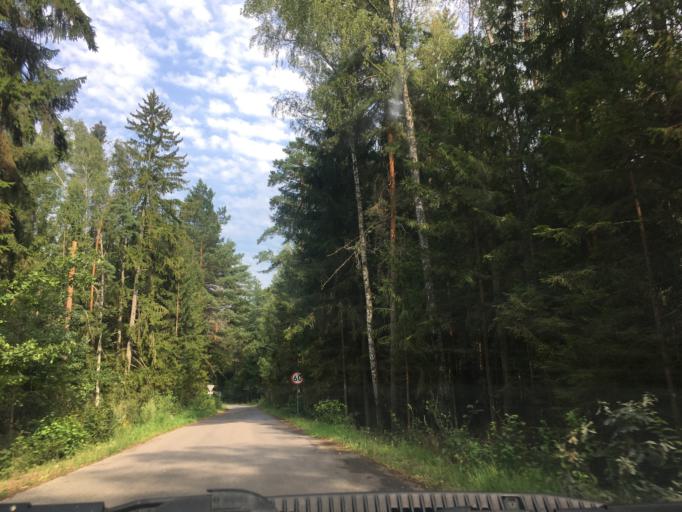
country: PL
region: Podlasie
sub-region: Powiat hajnowski
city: Bialowieza
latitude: 52.8820
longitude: 23.8408
